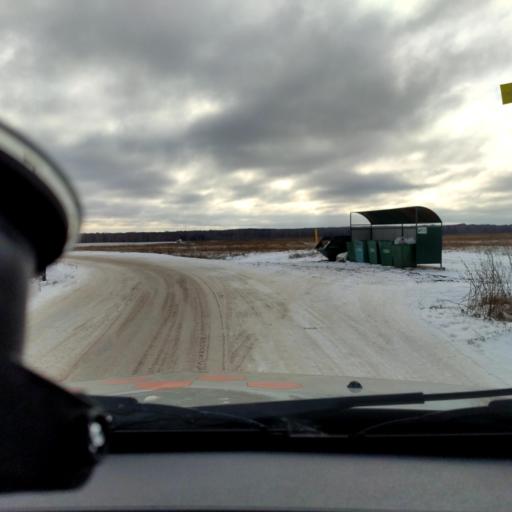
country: RU
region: Bashkortostan
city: Avdon
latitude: 54.7842
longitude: 55.7278
